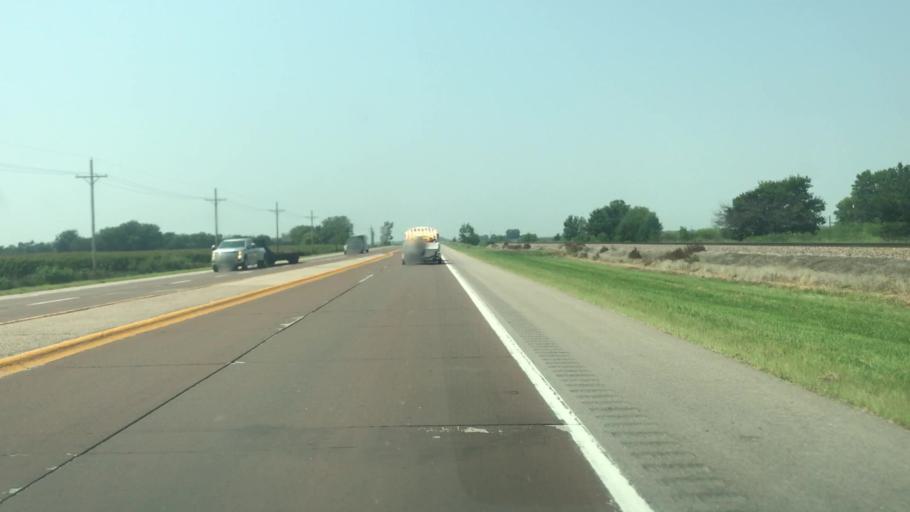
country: US
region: Nebraska
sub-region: Hall County
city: Grand Island
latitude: 40.9590
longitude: -98.4088
